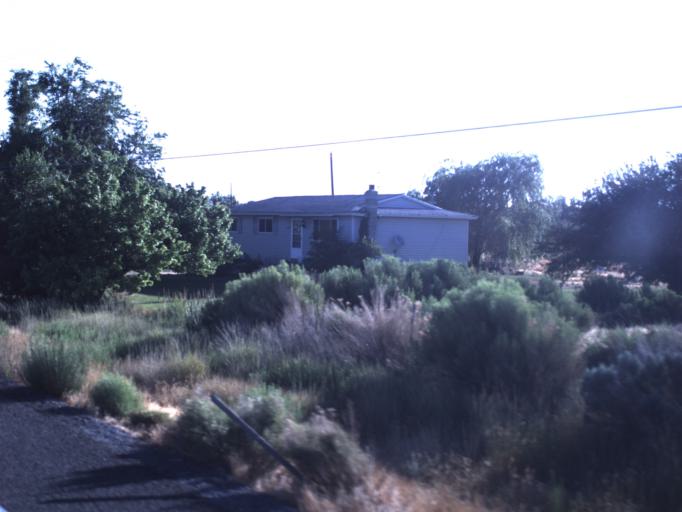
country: US
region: Utah
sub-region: Iron County
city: Enoch
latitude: 37.7532
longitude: -113.0552
